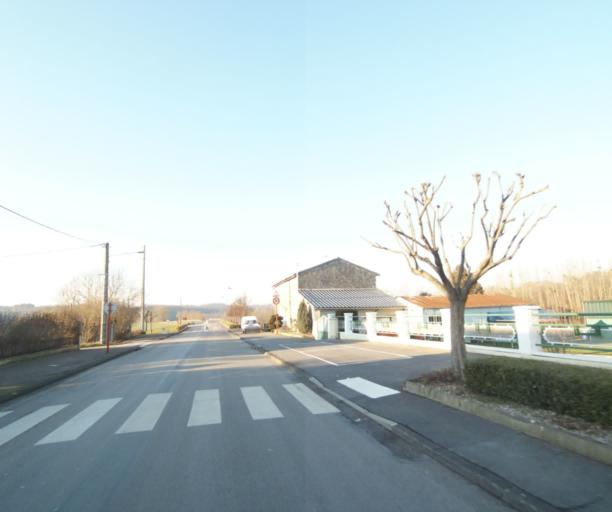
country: FR
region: Champagne-Ardenne
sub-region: Departement de la Haute-Marne
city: Bienville
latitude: 48.5632
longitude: 5.0495
